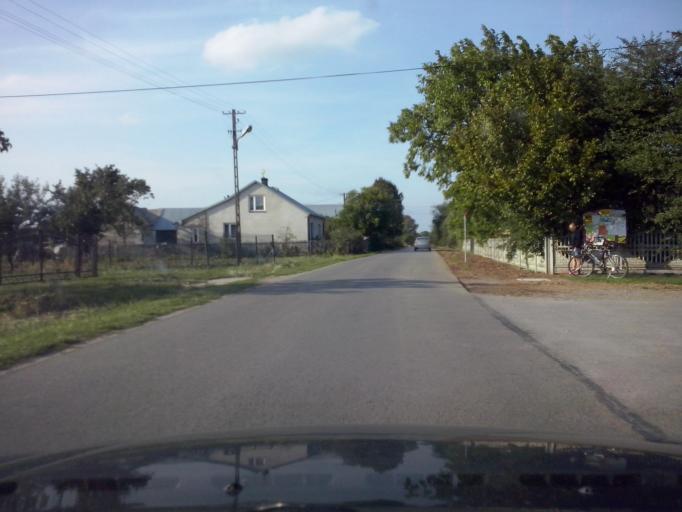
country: PL
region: Subcarpathian Voivodeship
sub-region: Powiat nizanski
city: Krzeszow
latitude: 50.3877
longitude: 22.3236
